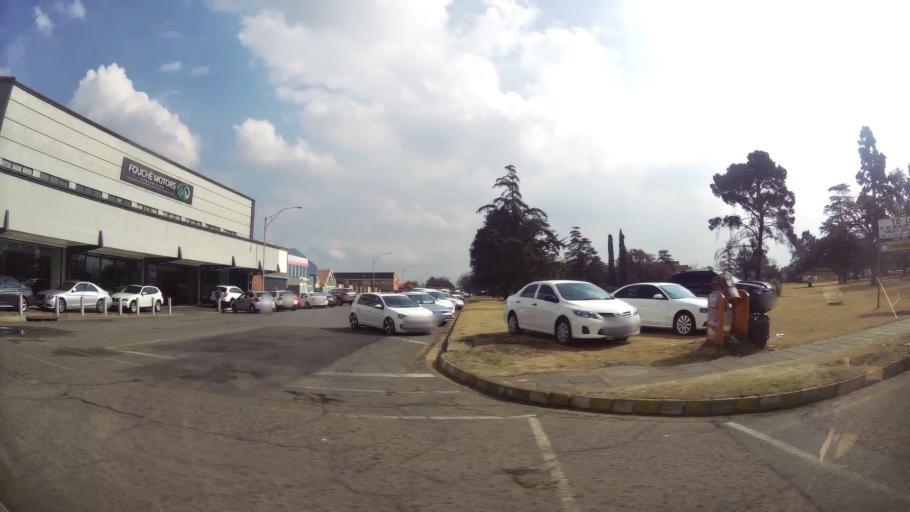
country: ZA
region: Gauteng
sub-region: Sedibeng District Municipality
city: Vereeniging
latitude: -26.6829
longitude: 27.9297
